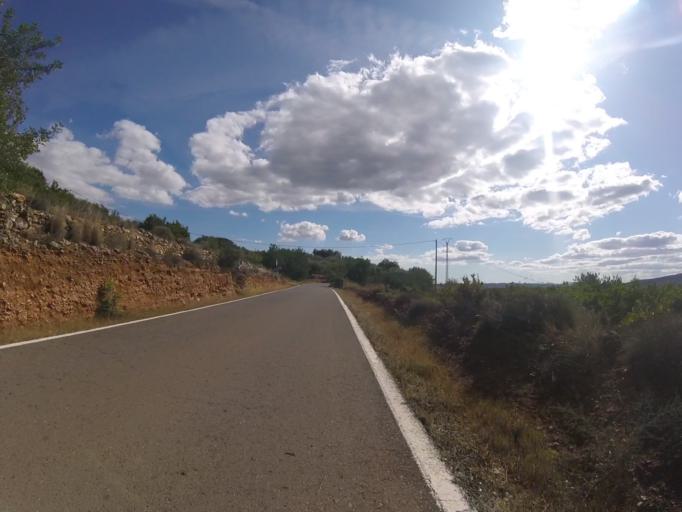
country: ES
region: Valencia
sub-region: Provincia de Castello
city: Cuevas de Vinroma
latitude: 40.3707
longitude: 0.1177
